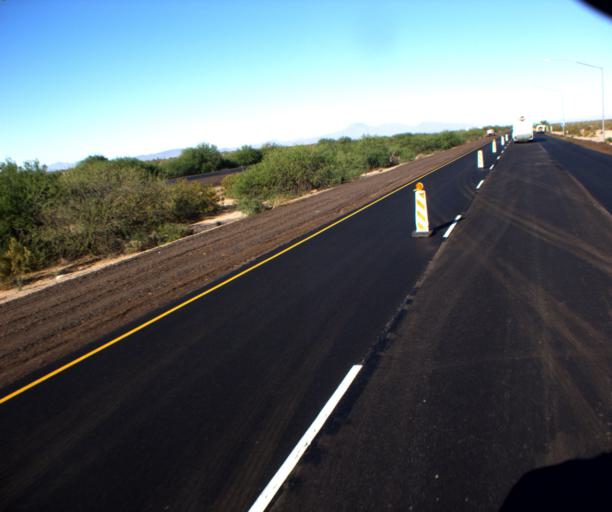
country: US
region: Arizona
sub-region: Pinal County
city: Casa Grande
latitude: 32.8282
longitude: -111.7817
